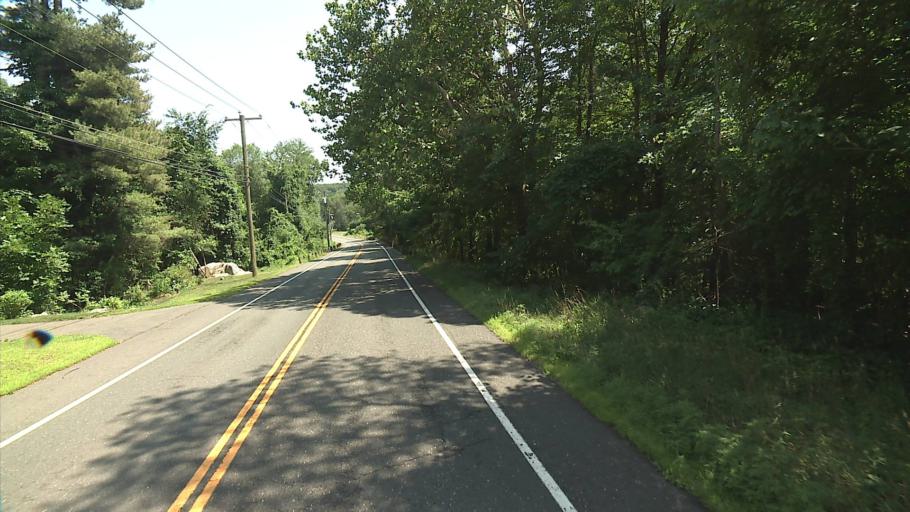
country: US
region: Connecticut
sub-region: Hartford County
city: North Granby
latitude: 41.9575
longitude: -72.8430
